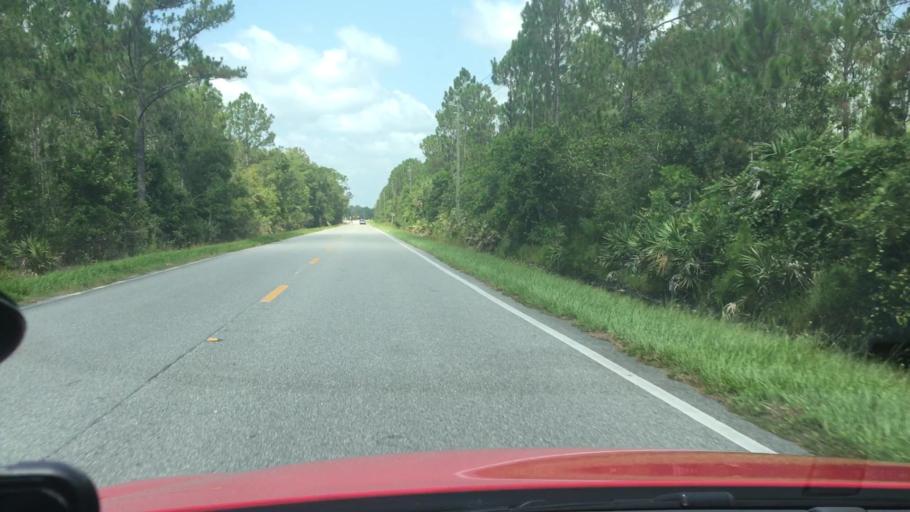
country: US
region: Florida
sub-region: Volusia County
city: Samsula-Spruce Creek
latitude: 29.0265
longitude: -81.1179
